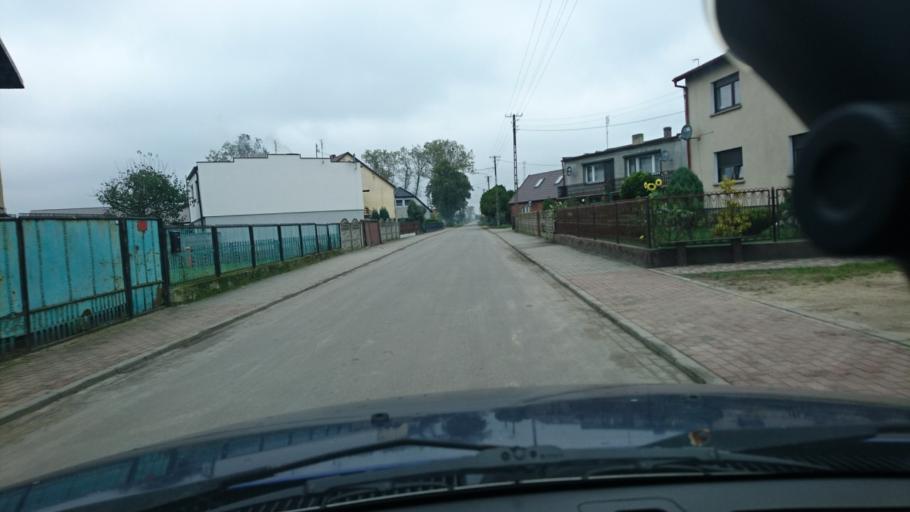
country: PL
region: Greater Poland Voivodeship
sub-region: Powiat krotoszynski
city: Sulmierzyce
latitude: 51.5657
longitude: 17.5839
